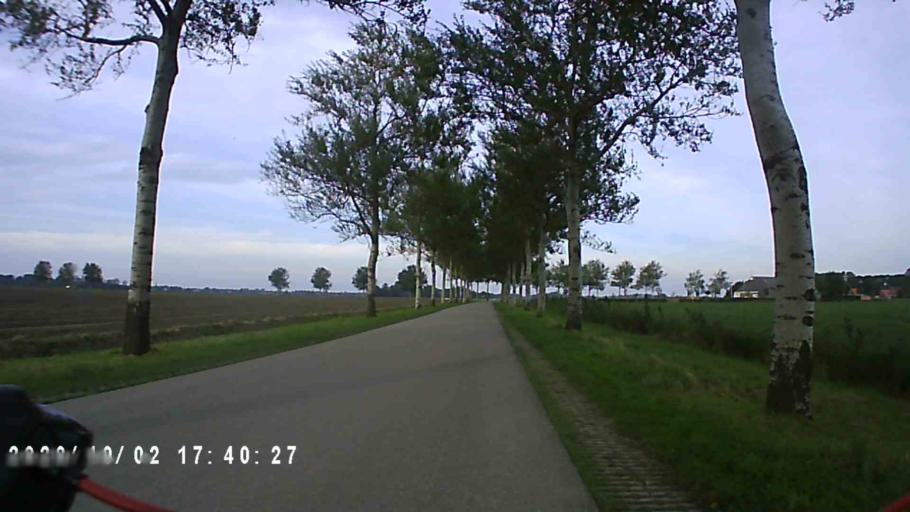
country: NL
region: Groningen
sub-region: Gemeente De Marne
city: Ulrum
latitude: 53.3374
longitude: 6.3697
